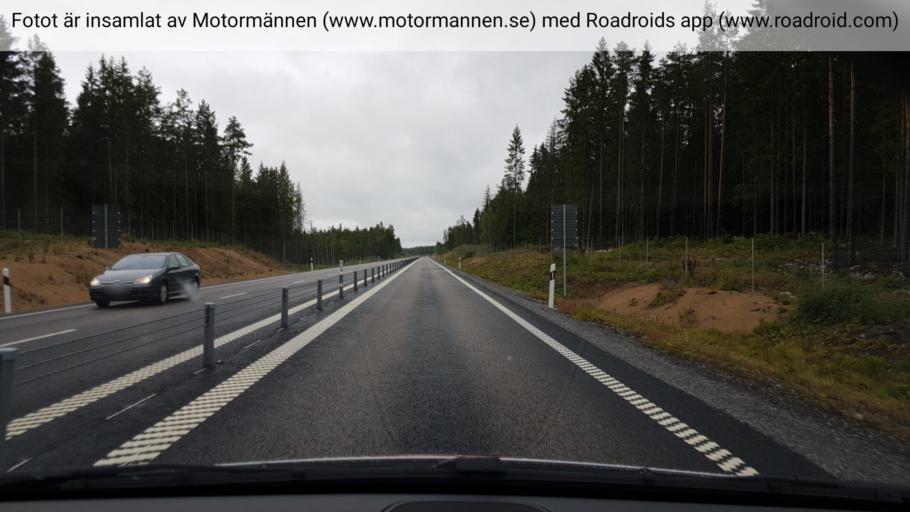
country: SE
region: Uppsala
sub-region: Heby Kommun
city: Tarnsjo
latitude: 60.1062
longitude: 16.9212
